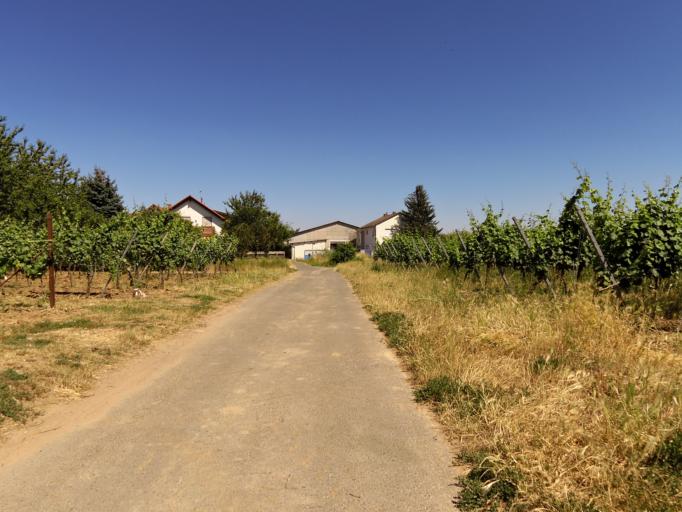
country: DE
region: Rheinland-Pfalz
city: Ruppertsberg
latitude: 49.3958
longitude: 8.1951
